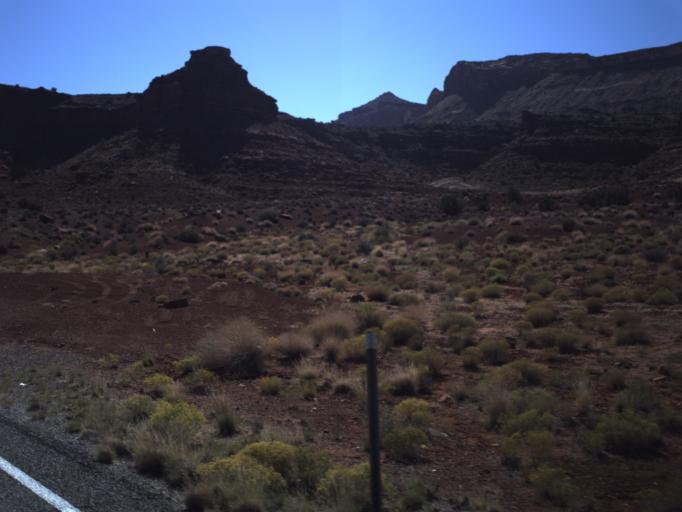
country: US
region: Utah
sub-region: San Juan County
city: Blanding
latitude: 37.8088
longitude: -110.3280
